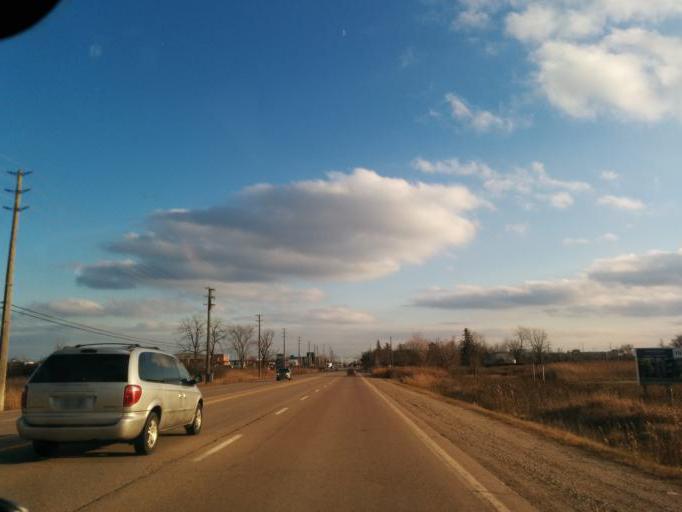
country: CA
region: Ontario
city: Oakville
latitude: 43.4909
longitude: -79.7238
